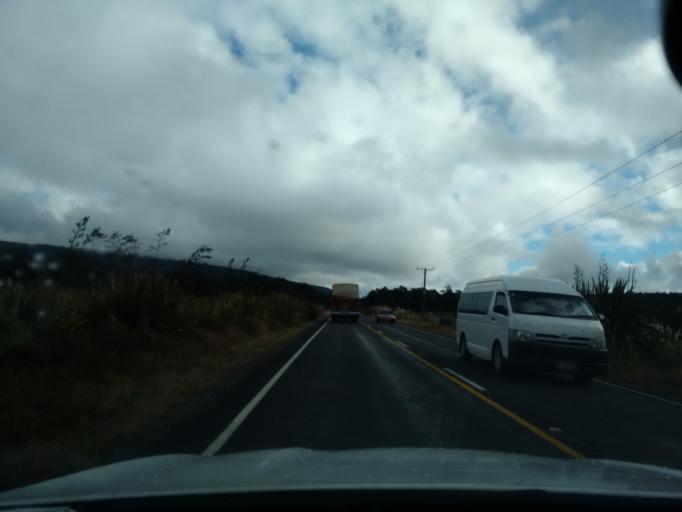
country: NZ
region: Manawatu-Wanganui
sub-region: Ruapehu District
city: Waiouru
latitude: -39.1718
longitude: 175.4771
